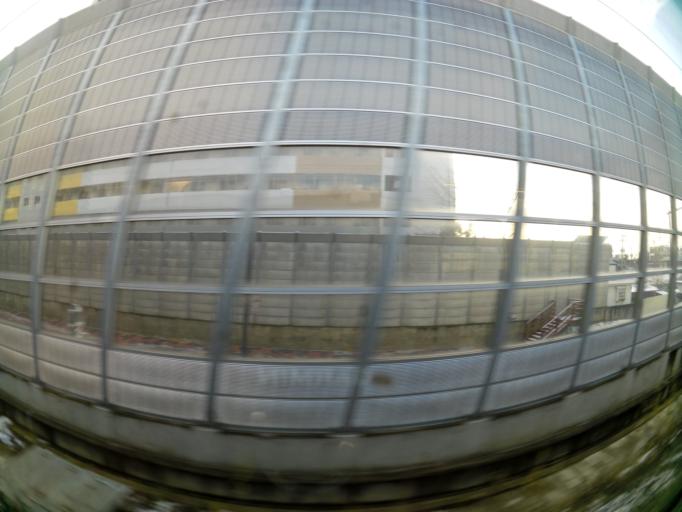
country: KR
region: Daejeon
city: Daejeon
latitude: 36.3444
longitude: 127.4253
